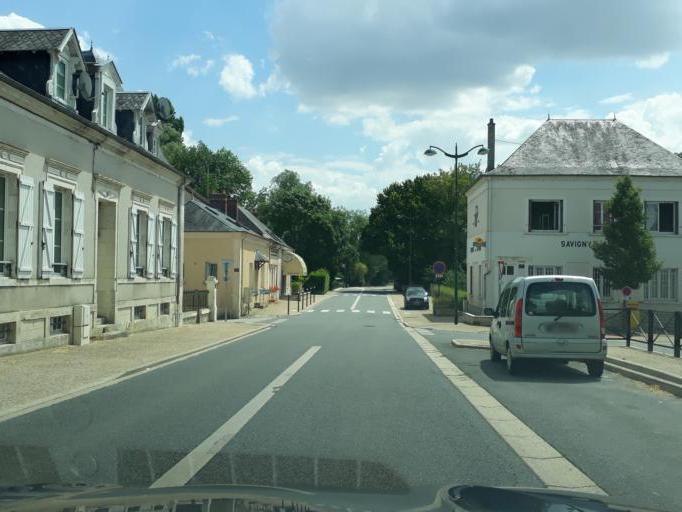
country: FR
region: Centre
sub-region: Departement du Cher
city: Avord
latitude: 47.0446
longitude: 2.5620
